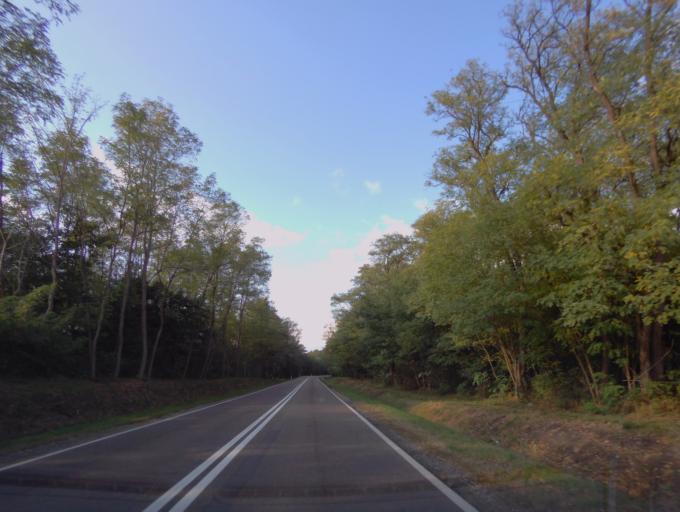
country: PL
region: Subcarpathian Voivodeship
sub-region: Powiat nizanski
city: Krzeszow
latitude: 50.3734
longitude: 22.3134
